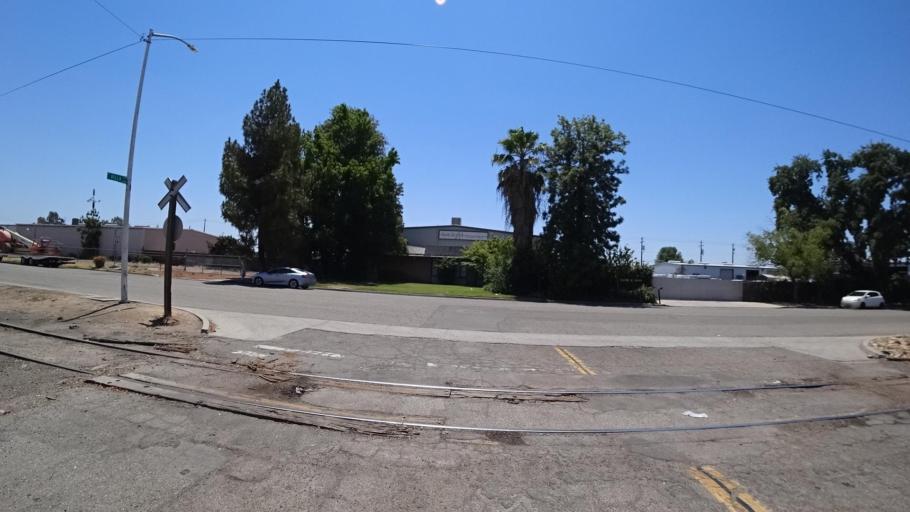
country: US
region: California
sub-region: Fresno County
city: Sunnyside
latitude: 36.7620
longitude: -119.7138
